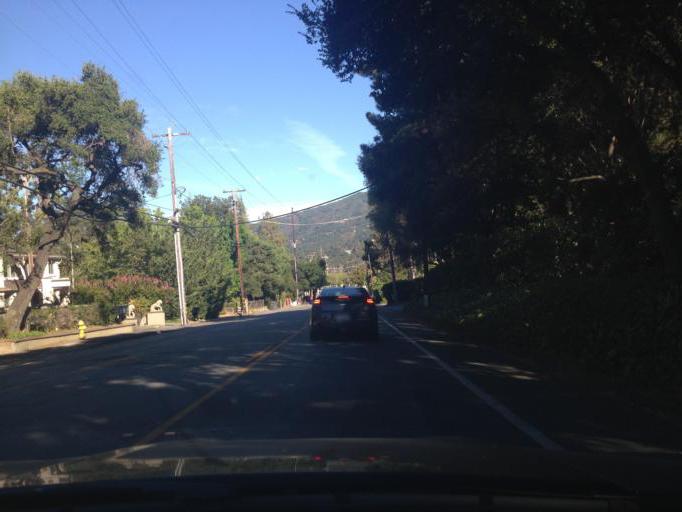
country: US
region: California
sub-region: Santa Clara County
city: Monte Sereno
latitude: 37.2320
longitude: -121.9857
